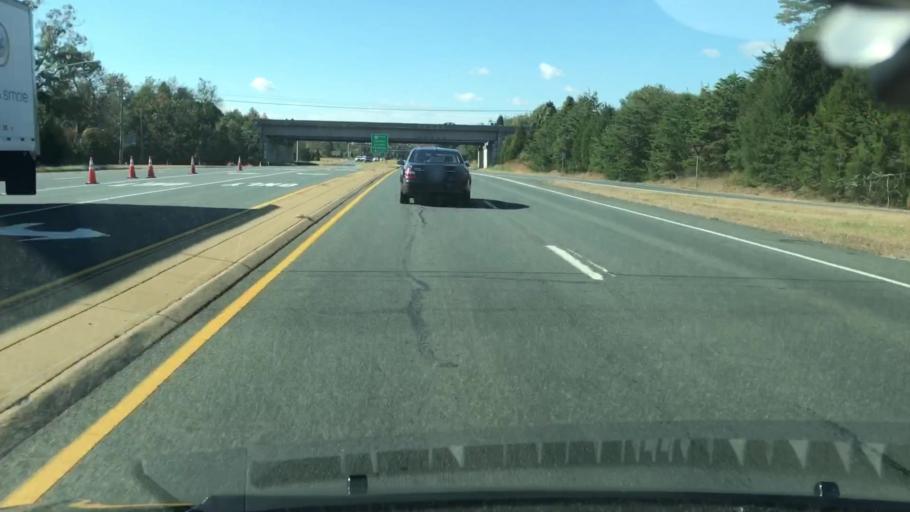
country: US
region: Virginia
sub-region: Fairfax County
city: Fairfax Station
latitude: 38.8296
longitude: -77.3652
